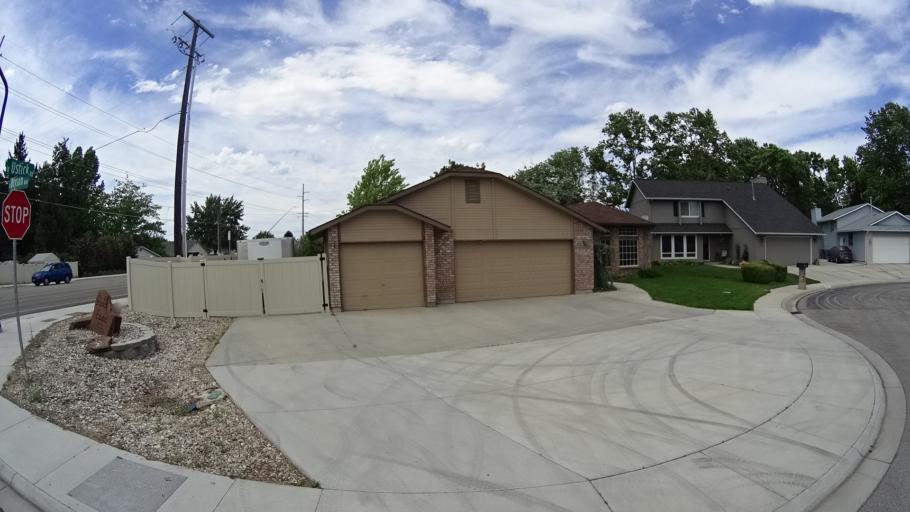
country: US
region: Idaho
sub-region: Ada County
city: Eagle
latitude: 43.6341
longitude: -116.3259
